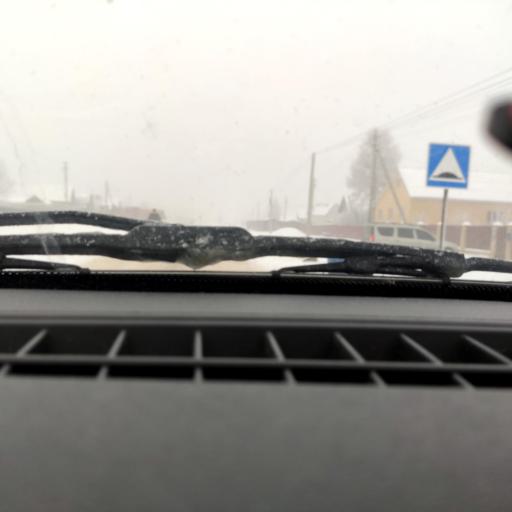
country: RU
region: Bashkortostan
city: Kabakovo
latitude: 54.6936
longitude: 56.1345
